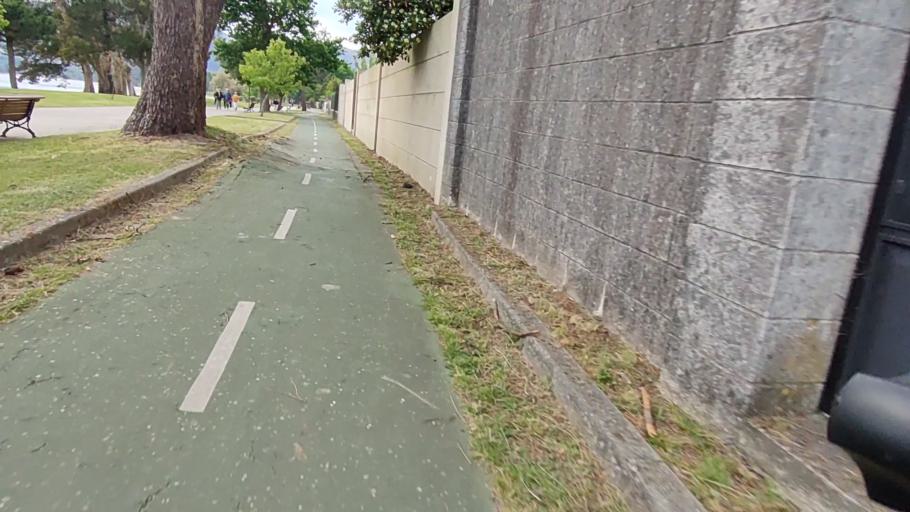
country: ES
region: Galicia
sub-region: Provincia da Coruna
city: Boiro
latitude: 42.6372
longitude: -8.8780
